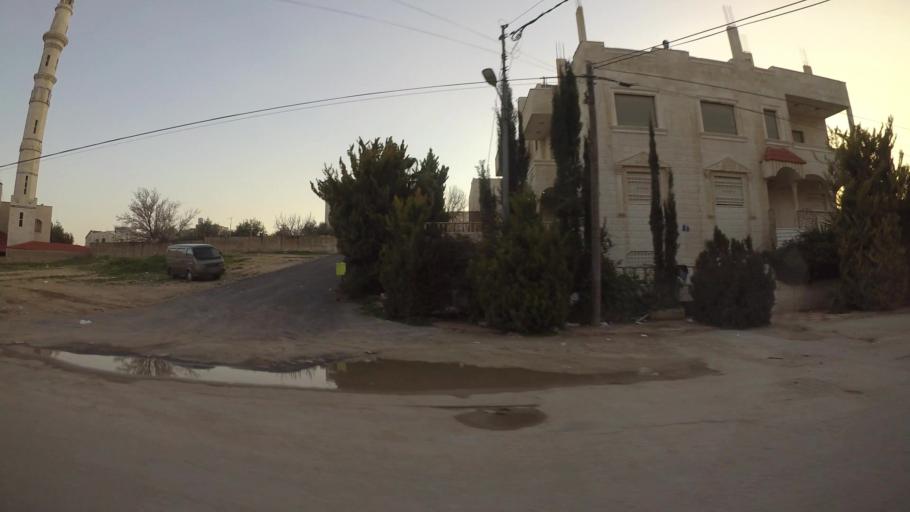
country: JO
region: Amman
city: Al Quwaysimah
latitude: 31.8988
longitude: 35.9293
